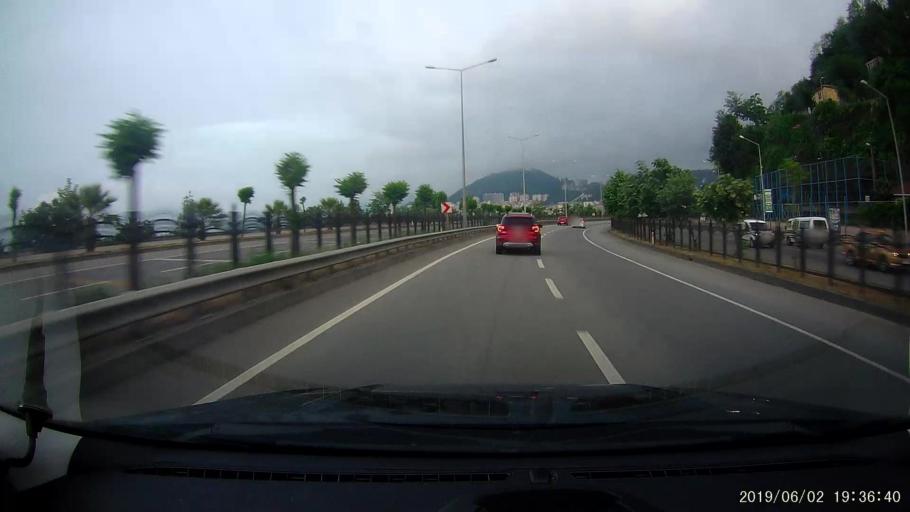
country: TR
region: Giresun
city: Giresun
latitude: 40.9245
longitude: 38.3910
